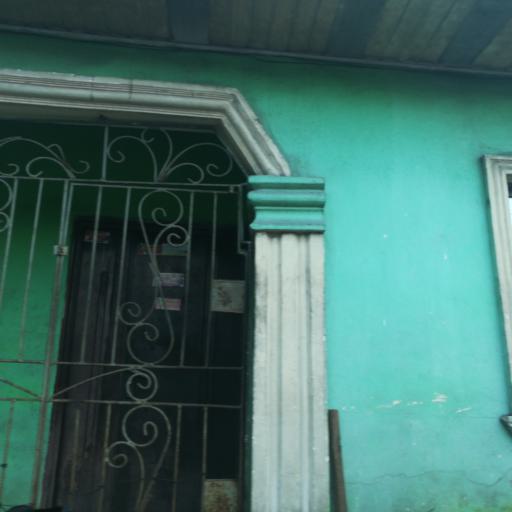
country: NG
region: Rivers
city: Port Harcourt
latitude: 4.7474
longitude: 7.0071
